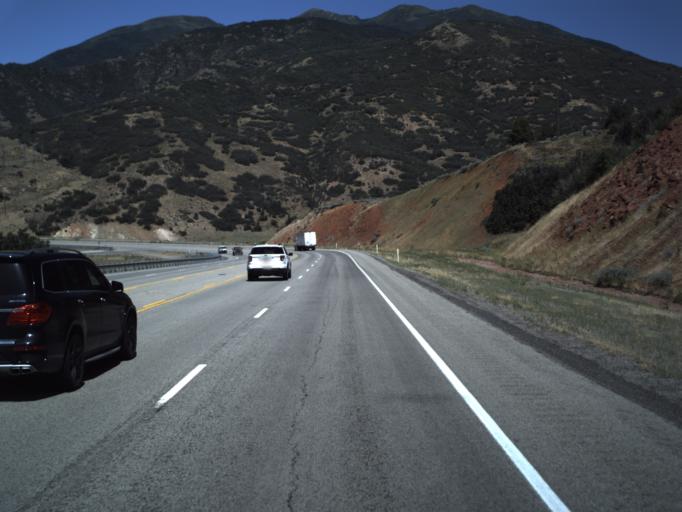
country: US
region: Utah
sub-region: Utah County
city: Mapleton
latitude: 40.0244
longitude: -111.4997
